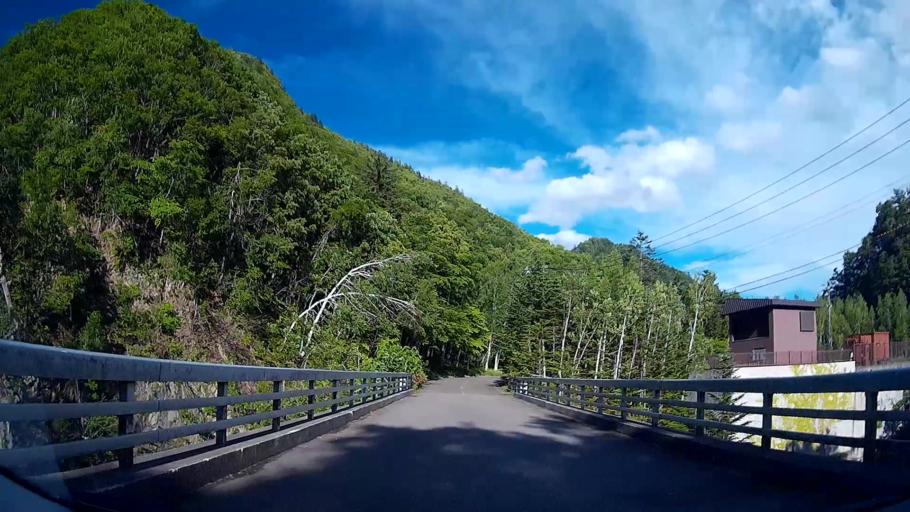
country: JP
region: Hokkaido
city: Sapporo
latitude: 42.9828
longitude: 141.1574
